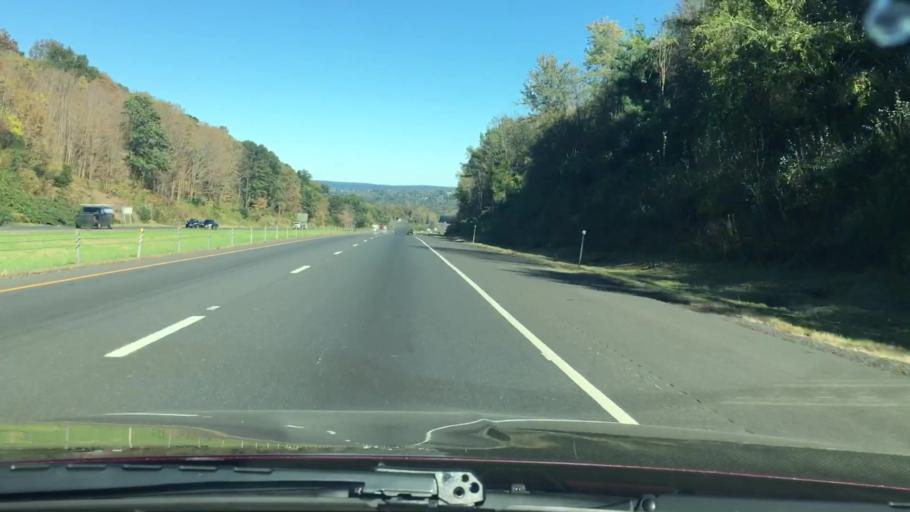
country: US
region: Connecticut
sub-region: New Haven County
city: Middlebury
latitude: 41.5143
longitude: -73.1200
